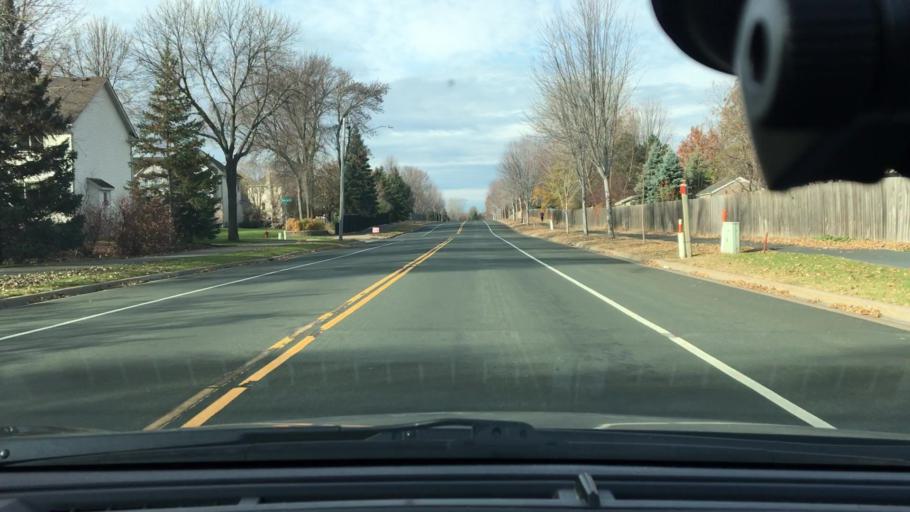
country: US
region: Minnesota
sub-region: Hennepin County
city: Corcoran
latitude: 45.1166
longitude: -93.5062
